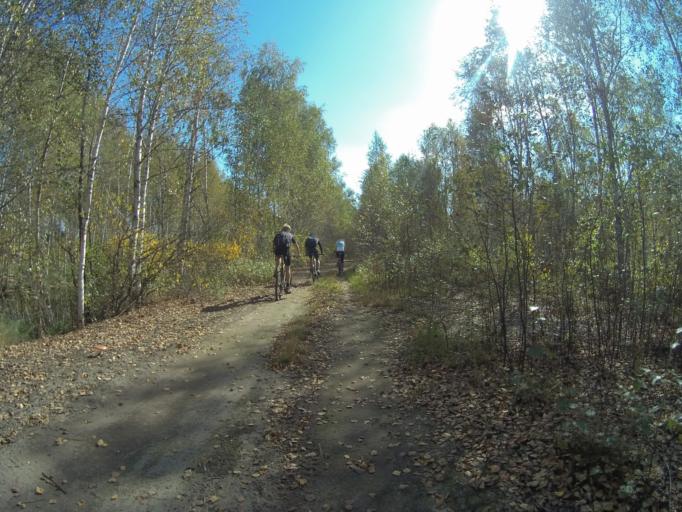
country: RU
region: Vladimir
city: Raduzhnyy
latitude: 55.8963
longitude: 40.2309
